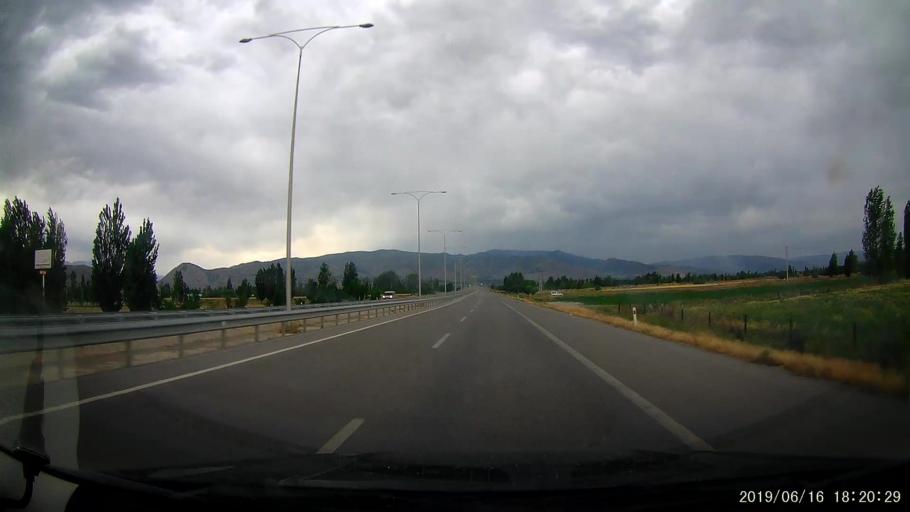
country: TR
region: Erzincan
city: Erzincan
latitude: 39.7201
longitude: 39.4681
